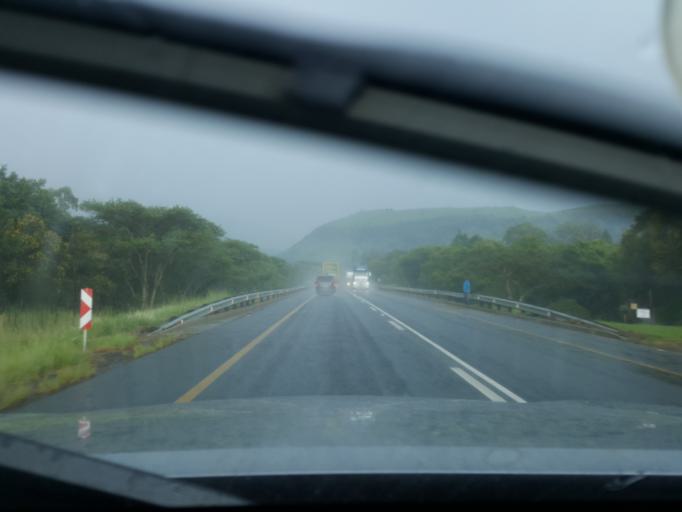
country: ZA
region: Mpumalanga
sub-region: Nkangala District Municipality
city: Belfast
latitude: -25.6100
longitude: 30.4291
